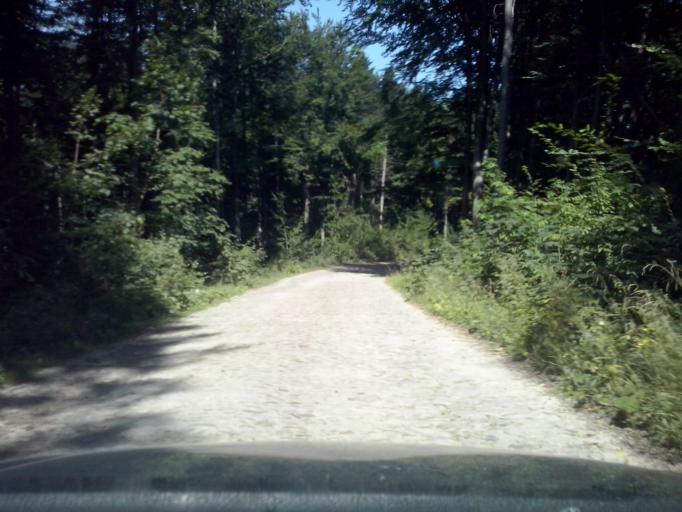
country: PL
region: Swietokrzyskie
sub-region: Powiat kielecki
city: Bieliny
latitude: 50.7881
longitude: 20.9336
